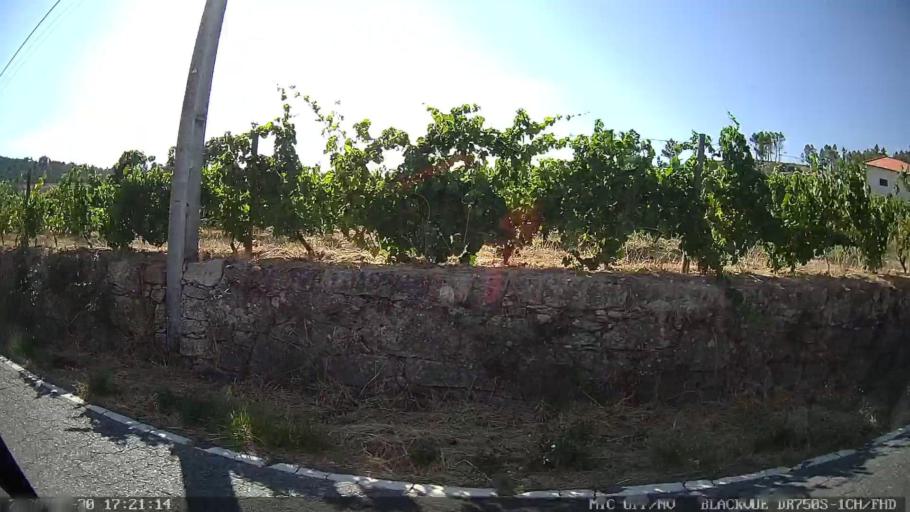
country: PT
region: Vila Real
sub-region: Sabrosa
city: Sabrosa
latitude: 41.2957
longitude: -7.4791
